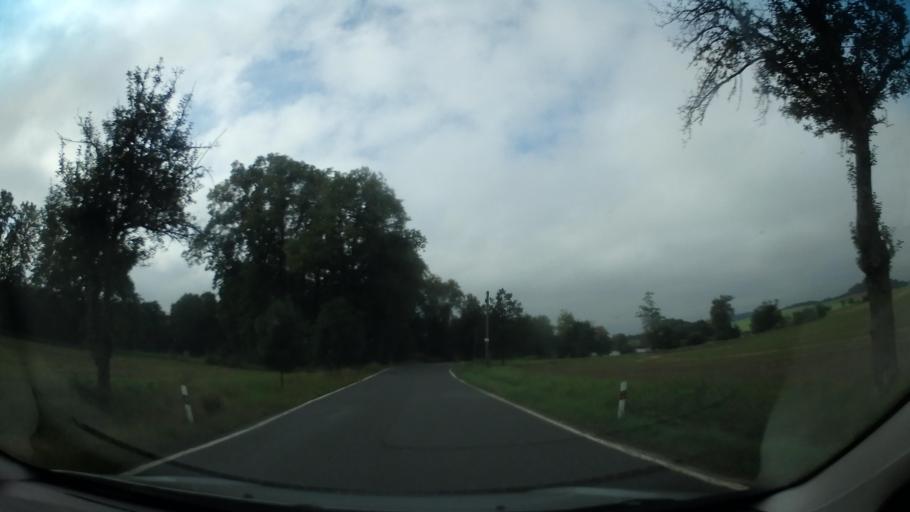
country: CZ
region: Central Bohemia
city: Sedlcany
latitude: 49.7010
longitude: 14.4416
